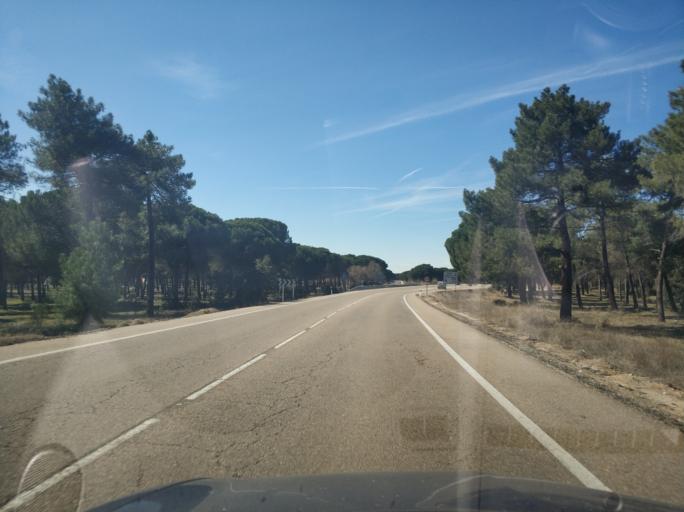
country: ES
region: Castille and Leon
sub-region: Provincia de Valladolid
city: Boecillo
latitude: 41.5324
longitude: -4.7251
